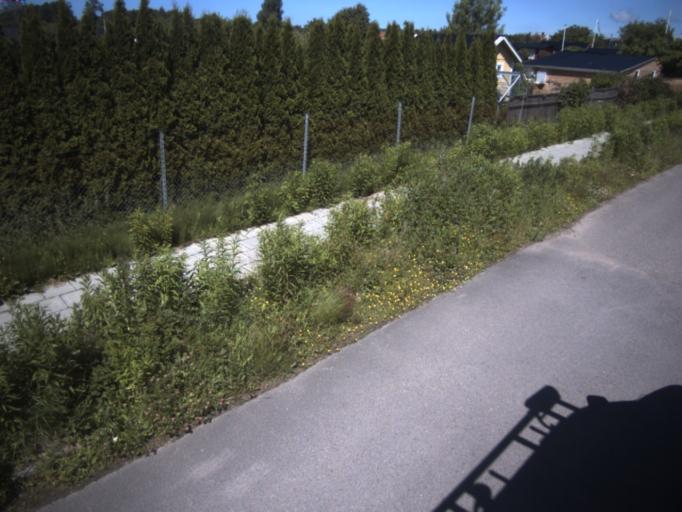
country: SE
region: Skane
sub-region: Helsingborg
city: Helsingborg
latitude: 56.0779
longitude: 12.6975
